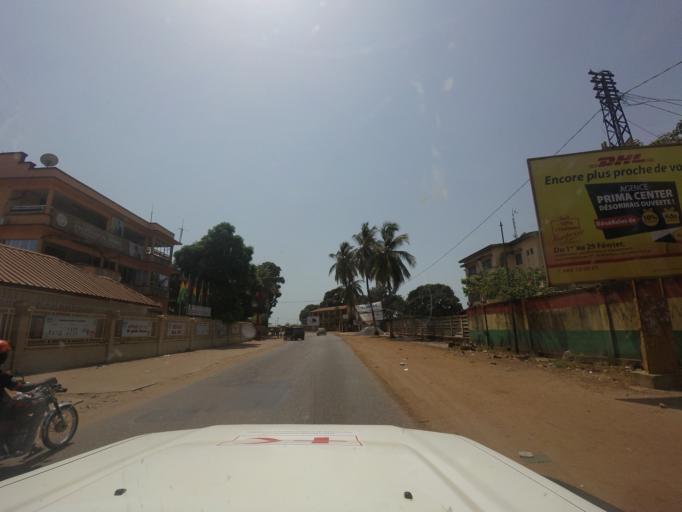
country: GN
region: Conakry
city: Camayenne
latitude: 9.5182
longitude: -13.7031
